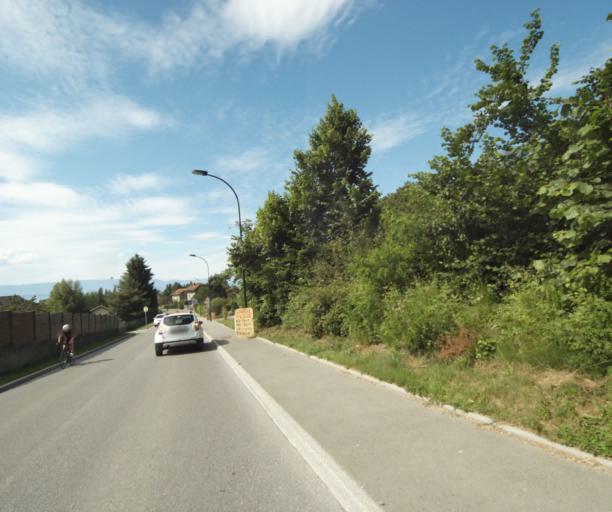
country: FR
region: Rhone-Alpes
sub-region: Departement de la Haute-Savoie
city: Thonon-les-Bains
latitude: 46.3501
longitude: 6.4790
